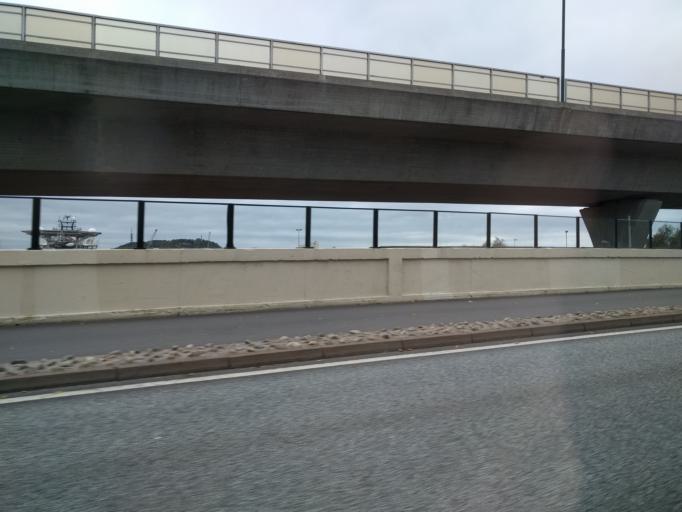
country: NO
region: Vest-Agder
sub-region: Kristiansand
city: Kristiansand
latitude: 58.1461
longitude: 7.9834
